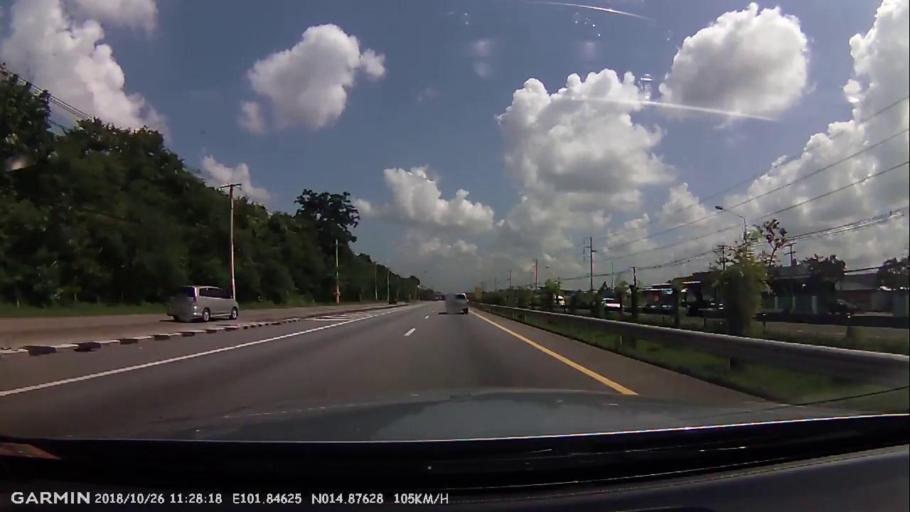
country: TH
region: Nakhon Ratchasima
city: Sung Noen
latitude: 14.8769
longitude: 101.8458
